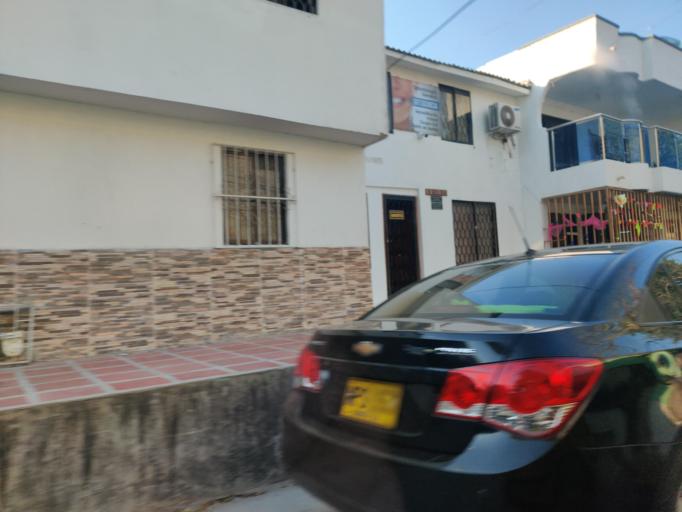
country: CO
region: Atlantico
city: Soledad
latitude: 10.9125
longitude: -74.8027
